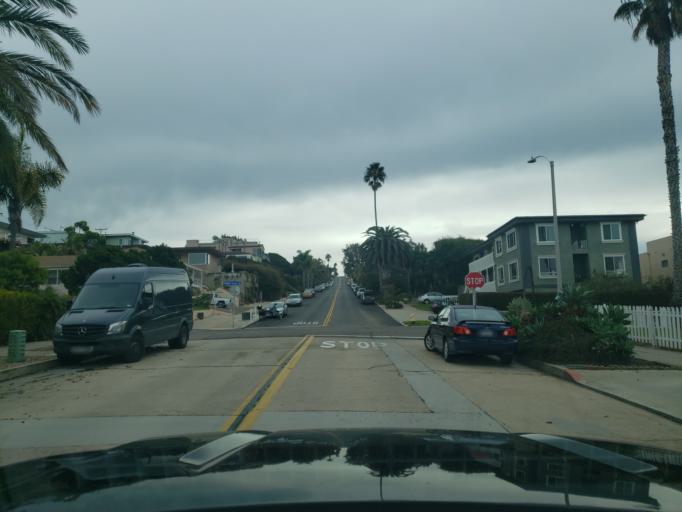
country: US
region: California
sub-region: San Diego County
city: Coronado
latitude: 32.7407
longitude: -117.2515
